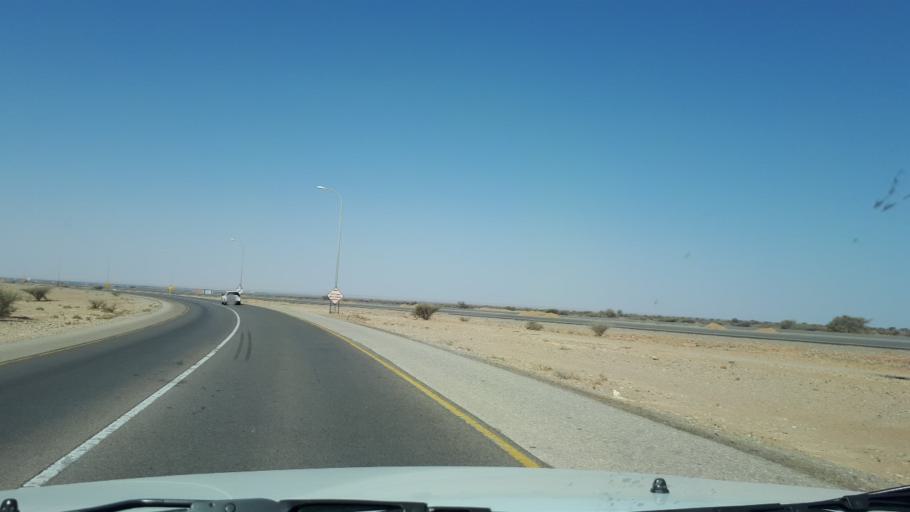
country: OM
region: Ash Sharqiyah
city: Sur
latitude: 22.3155
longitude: 59.2949
